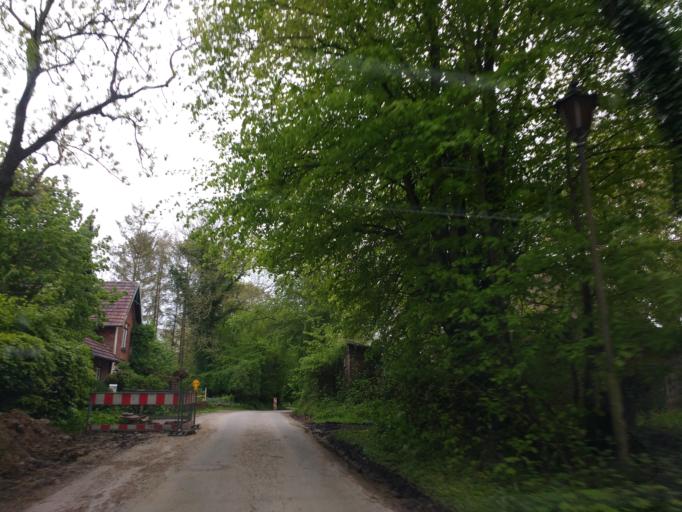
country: DE
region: Schleswig-Holstein
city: Damp
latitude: 54.5790
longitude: 9.9797
